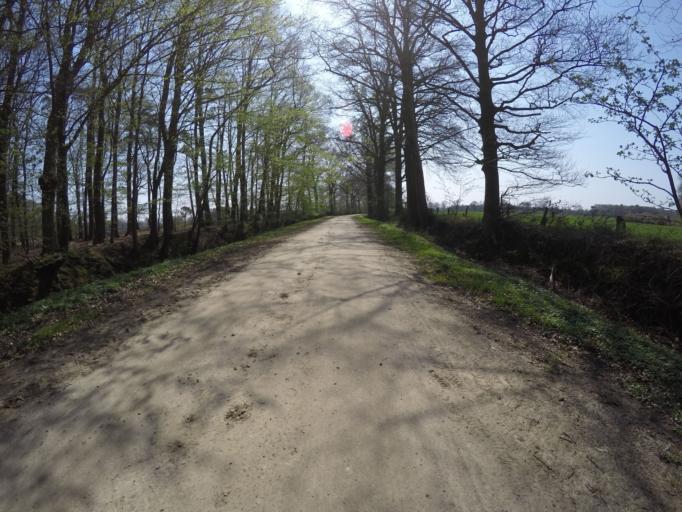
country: DE
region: Schleswig-Holstein
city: Borstel-Hohenraden
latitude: 53.7210
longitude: 9.8314
